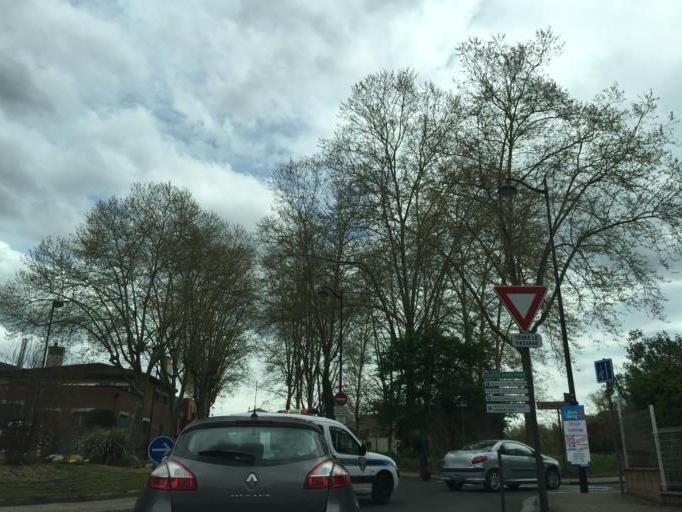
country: FR
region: Midi-Pyrenees
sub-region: Departement du Tarn
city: Albi
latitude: 43.9252
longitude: 2.1406
